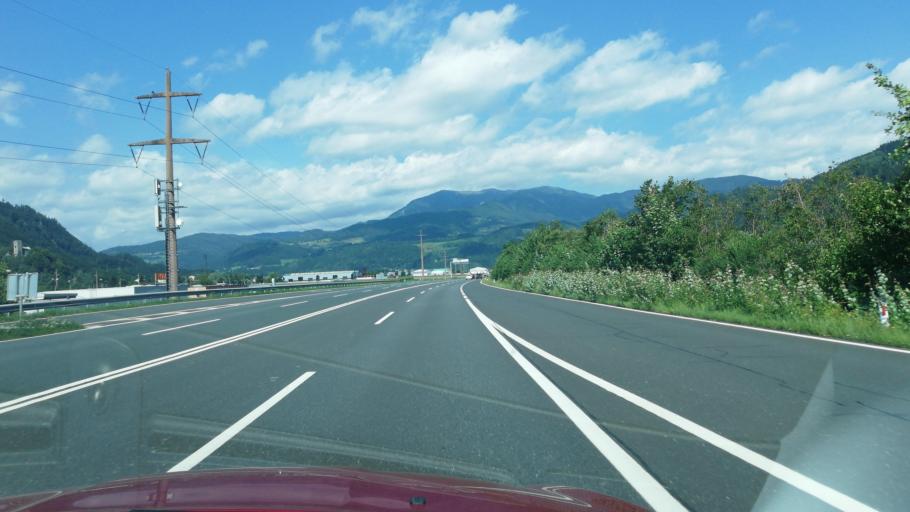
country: AT
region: Carinthia
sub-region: Politischer Bezirk Sankt Veit an der Glan
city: Friesach
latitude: 46.9529
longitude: 14.4154
